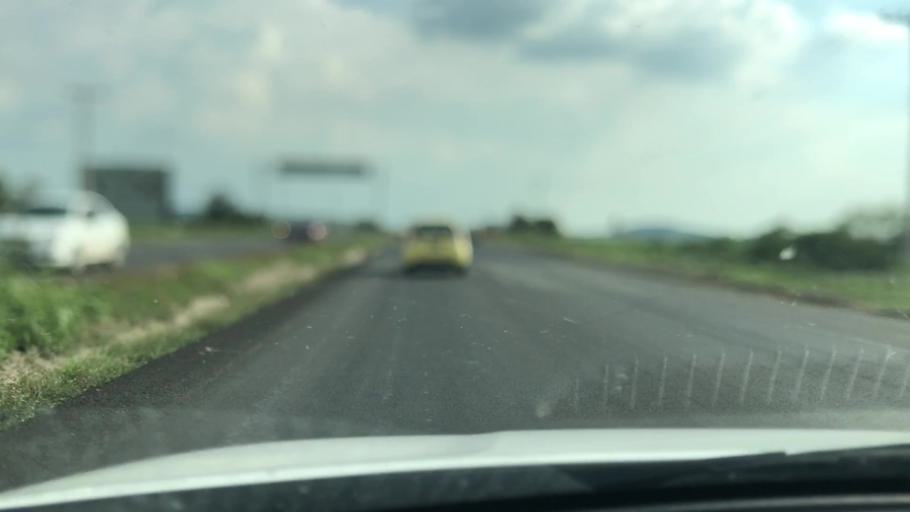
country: MX
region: Guanajuato
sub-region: Irapuato
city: Colonia Morelos de Guadalupe de Rivera
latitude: 20.5907
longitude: -101.4257
